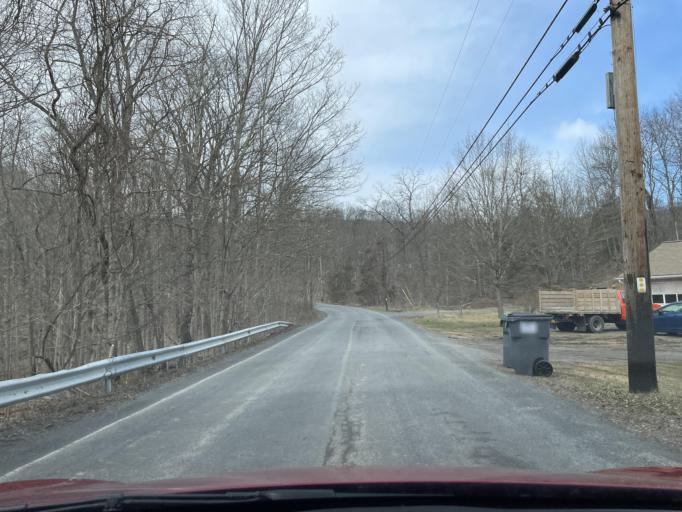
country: US
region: New York
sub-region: Ulster County
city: Saugerties
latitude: 42.1028
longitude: -73.9780
